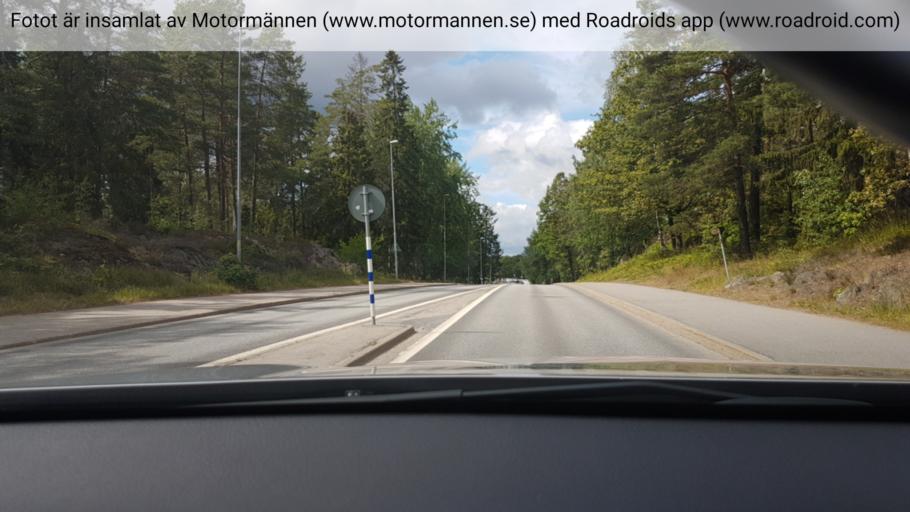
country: SE
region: Stockholm
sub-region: Tyreso Kommun
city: Bollmora
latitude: 59.2369
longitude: 18.2223
